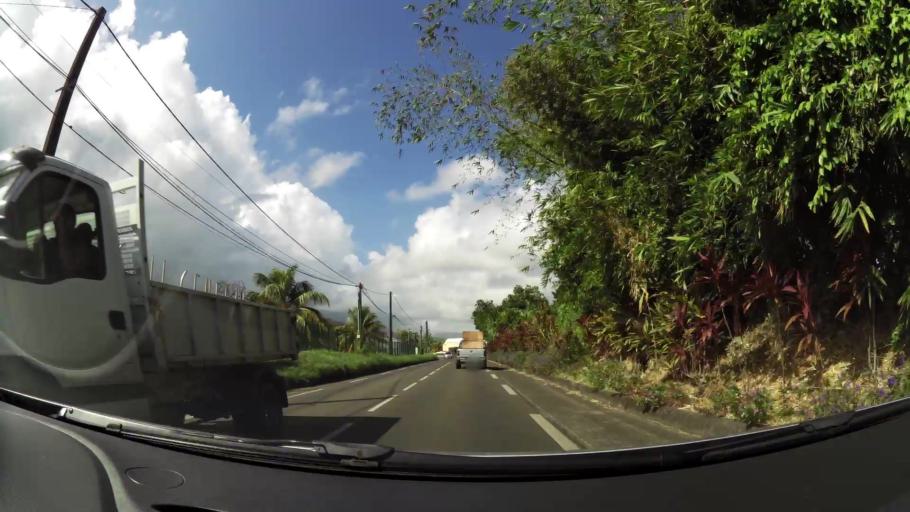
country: MQ
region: Martinique
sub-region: Martinique
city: Le Lorrain
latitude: 14.8443
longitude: -61.0860
